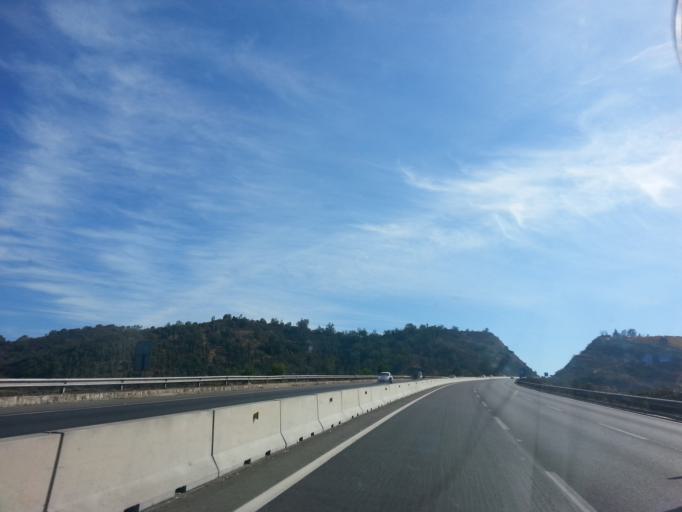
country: CL
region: Valparaiso
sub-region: Provincia de Marga Marga
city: Quilpue
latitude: -33.2924
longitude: -71.4226
